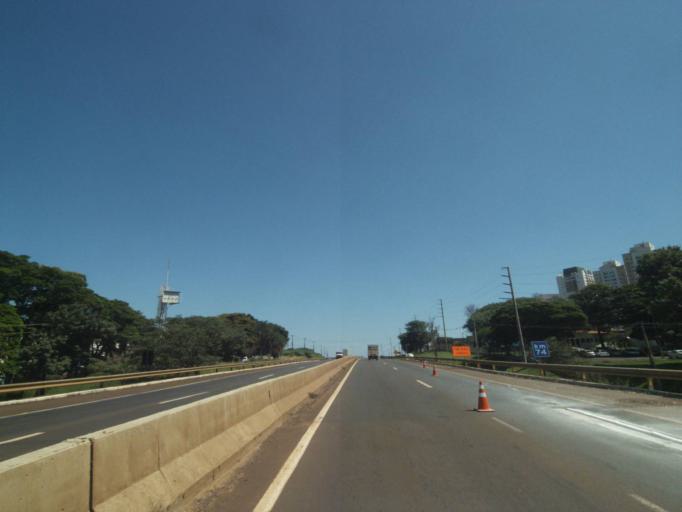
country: BR
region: Parana
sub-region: Londrina
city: Londrina
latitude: -23.3369
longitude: -51.1839
